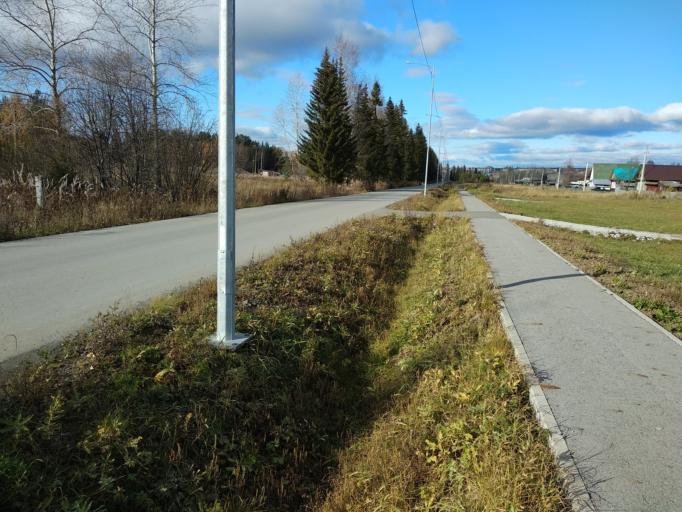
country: RU
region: Sverdlovsk
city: Volchansk
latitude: 59.9205
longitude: 60.0943
